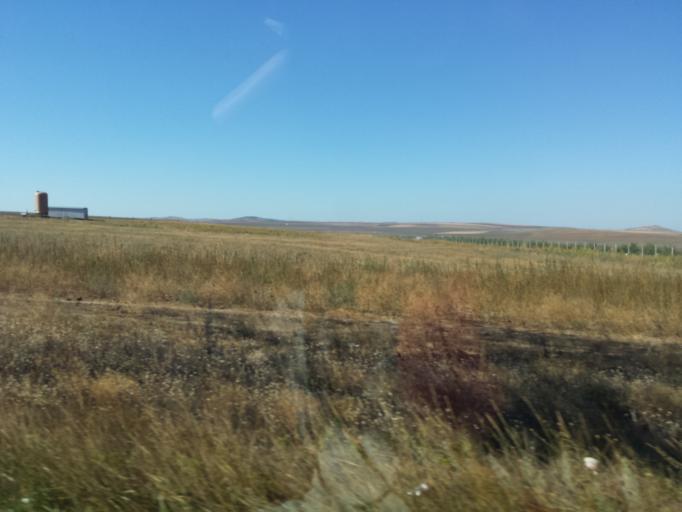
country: RO
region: Tulcea
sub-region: Comuna Frecatei
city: Cataloi
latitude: 45.0855
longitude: 28.7111
